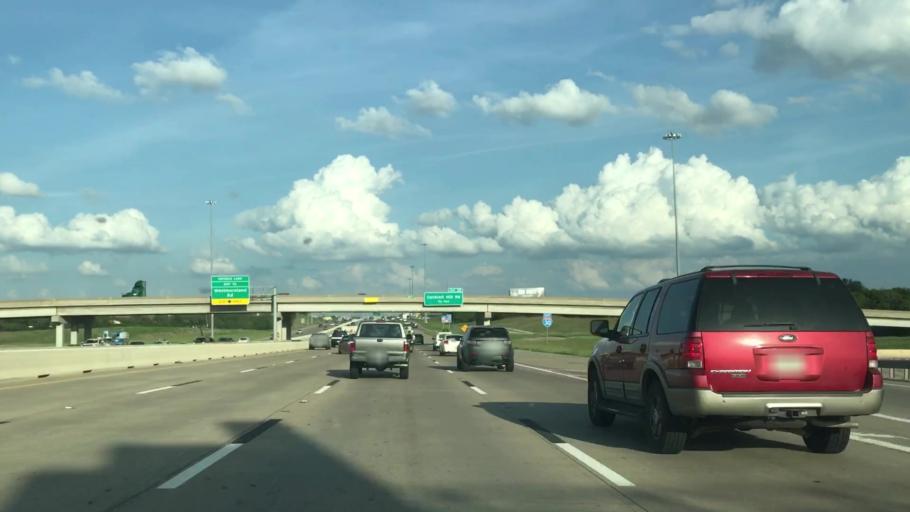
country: US
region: Texas
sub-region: Dallas County
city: Cockrell Hill
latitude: 32.7662
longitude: -96.9117
